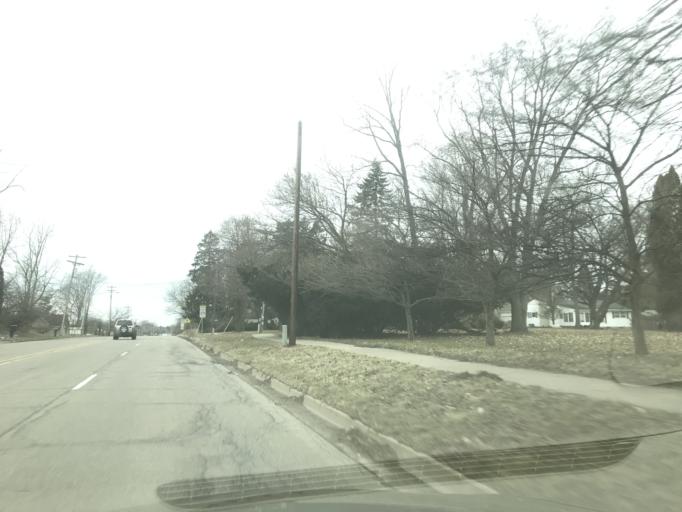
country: US
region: Michigan
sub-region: Ingham County
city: East Lansing
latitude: 42.7553
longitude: -84.4568
